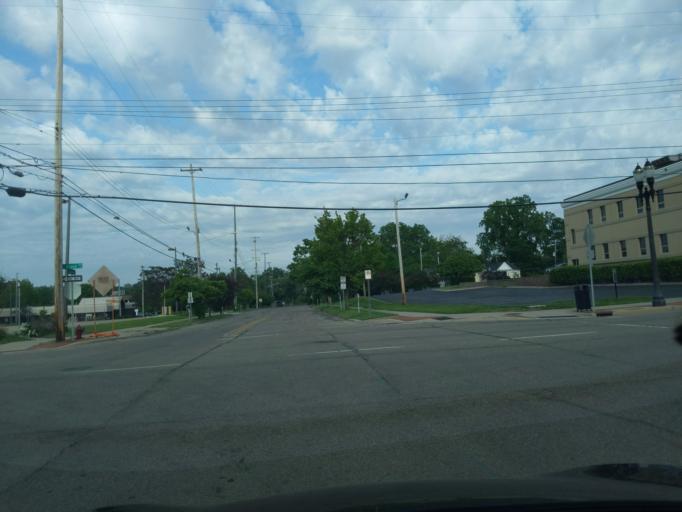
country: US
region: Michigan
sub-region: Ingham County
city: Lansing
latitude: 42.7286
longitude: -84.5509
